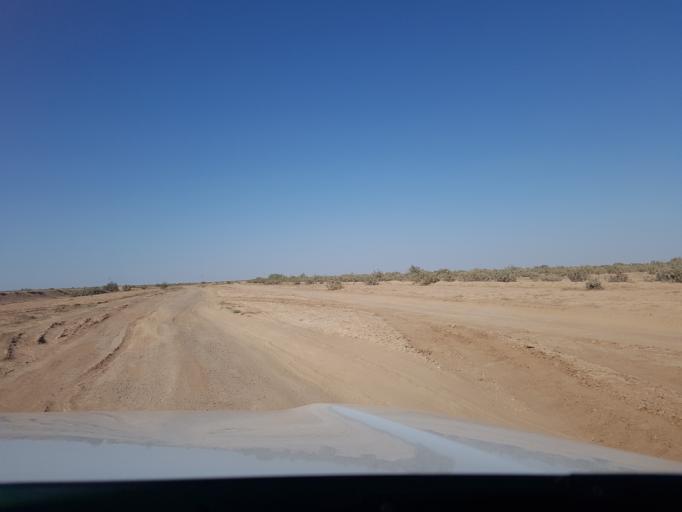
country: IR
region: Razavi Khorasan
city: Sarakhs
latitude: 36.8407
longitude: 61.3336
